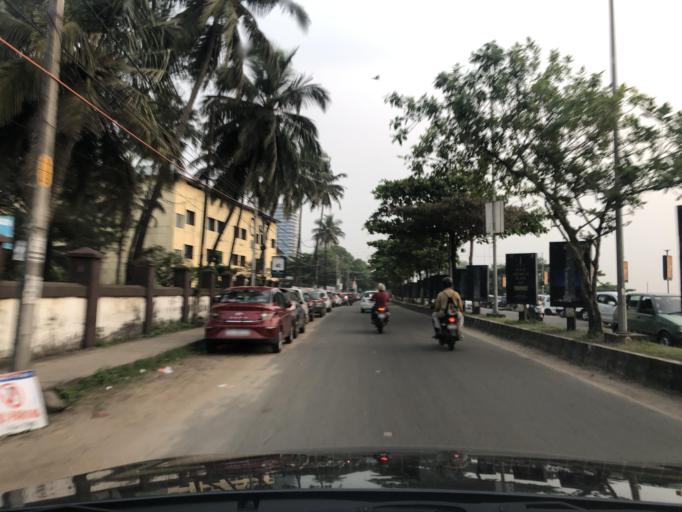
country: IN
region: Kerala
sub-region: Kozhikode
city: Kozhikode
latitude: 11.2581
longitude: 75.7694
